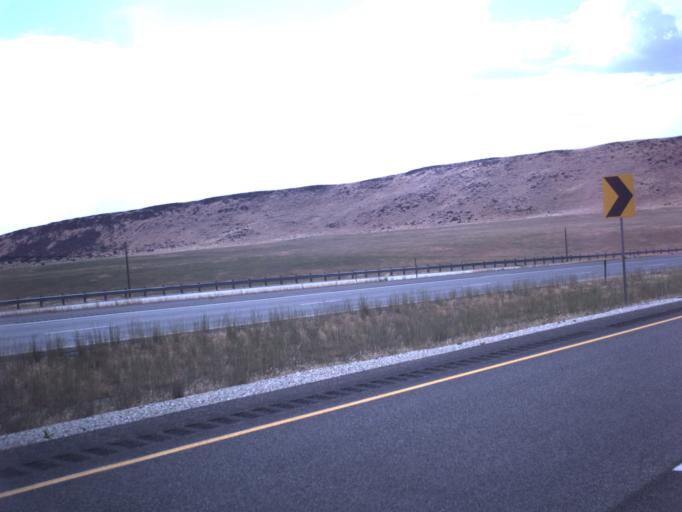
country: US
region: Idaho
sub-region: Oneida County
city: Malad City
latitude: 41.8969
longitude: -112.5760
